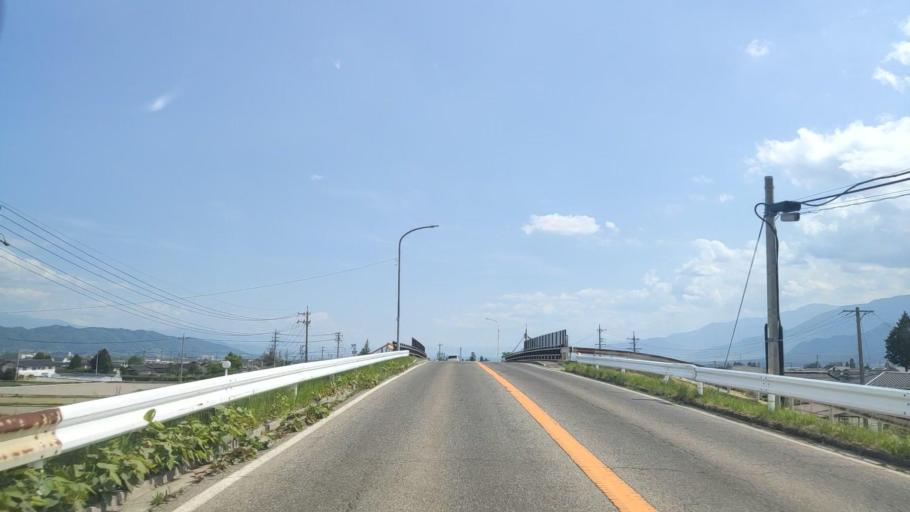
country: JP
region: Nagano
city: Omachi
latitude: 36.4515
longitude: 137.8523
